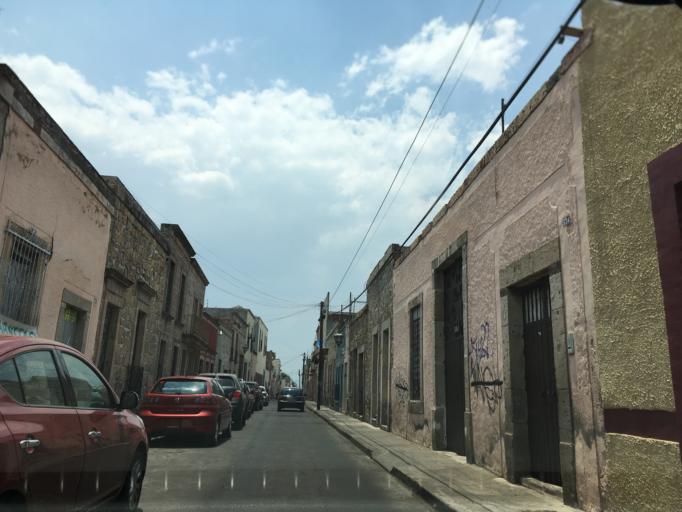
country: MX
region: Michoacan
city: Morelia
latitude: 19.6989
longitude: -101.1973
